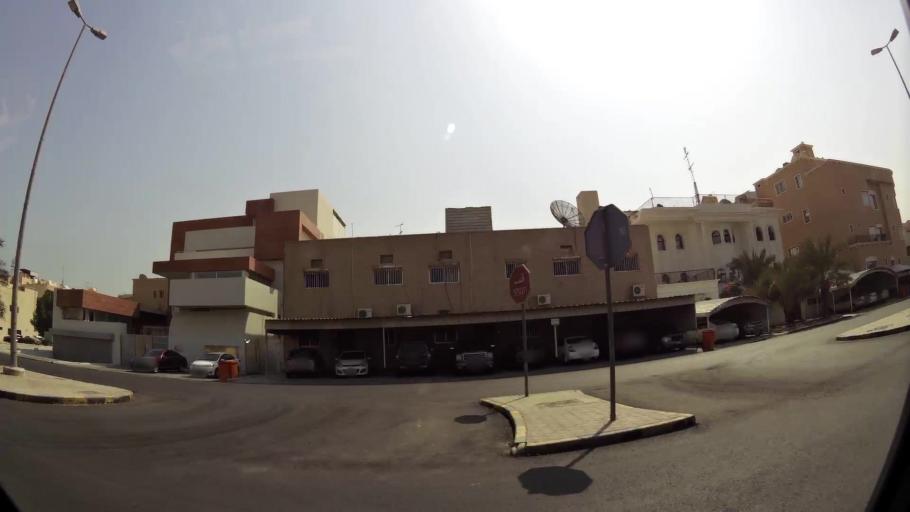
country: KW
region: Al Asimah
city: Ad Dasmah
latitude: 29.3481
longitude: 48.0046
